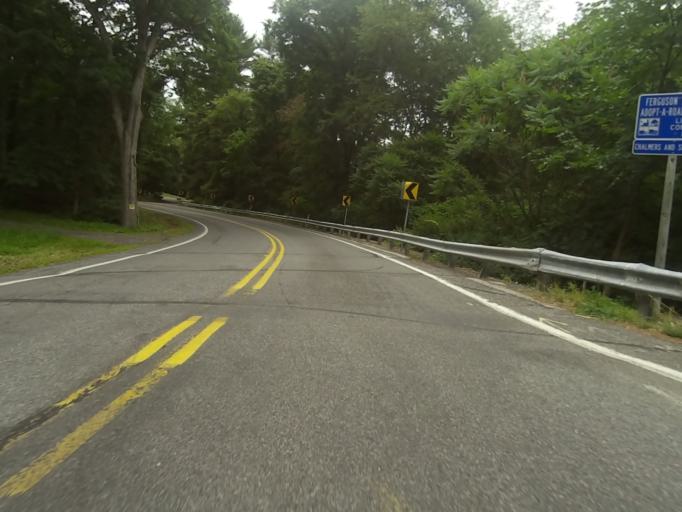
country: US
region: Pennsylvania
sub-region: Centre County
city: Pine Grove Mills
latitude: 40.7439
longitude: -77.9554
